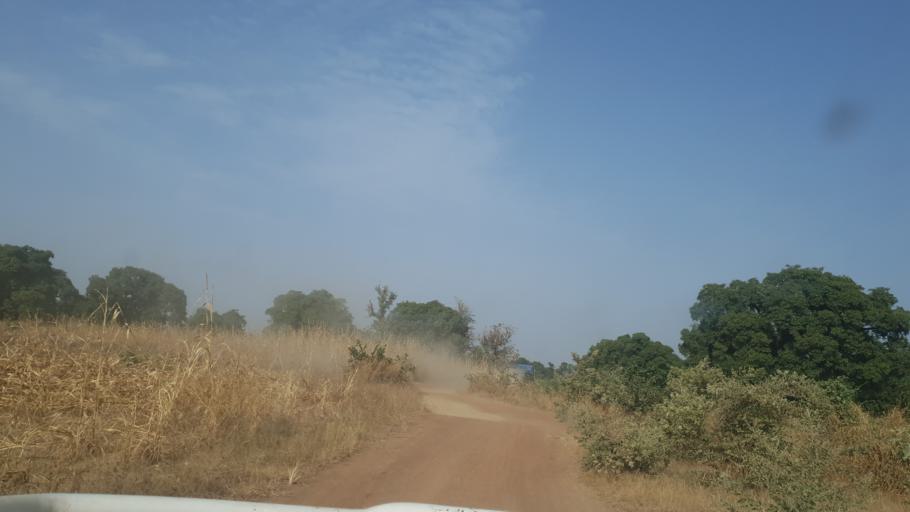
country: ML
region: Segou
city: Baroueli
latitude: 13.3479
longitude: -6.9440
